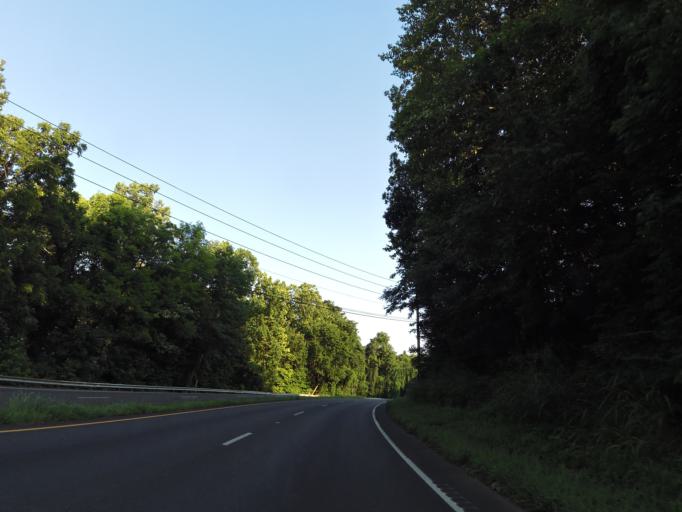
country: US
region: Tennessee
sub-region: Knox County
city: Knoxville
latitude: 36.0130
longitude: -84.0328
